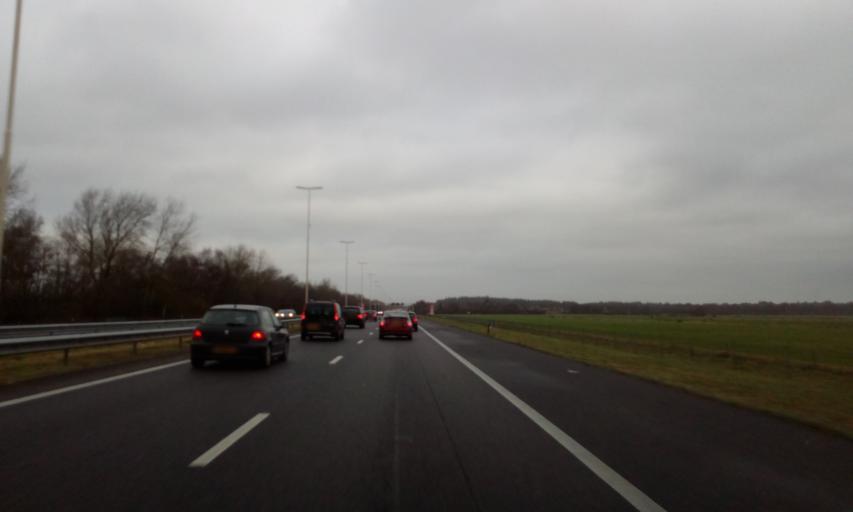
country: NL
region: North Holland
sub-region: Gemeente Wijdemeren
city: Nieuw-Loosdrecht
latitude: 52.1645
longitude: 5.1720
